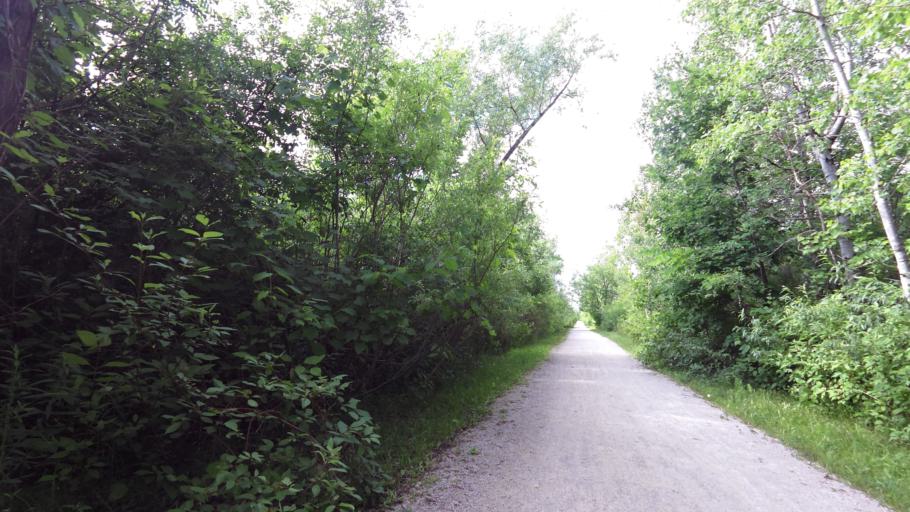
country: CA
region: Ontario
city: Brampton
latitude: 43.8010
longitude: -79.9318
